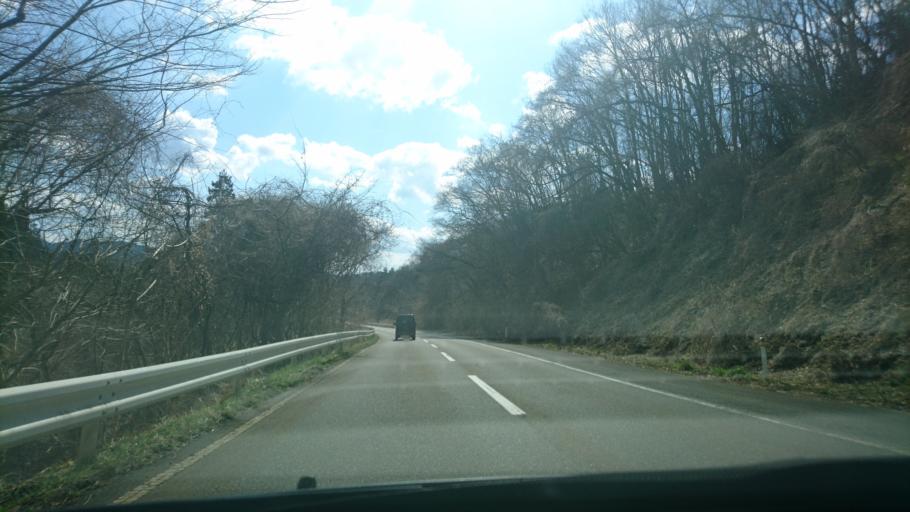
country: JP
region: Iwate
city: Kitakami
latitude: 39.3088
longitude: 141.2096
